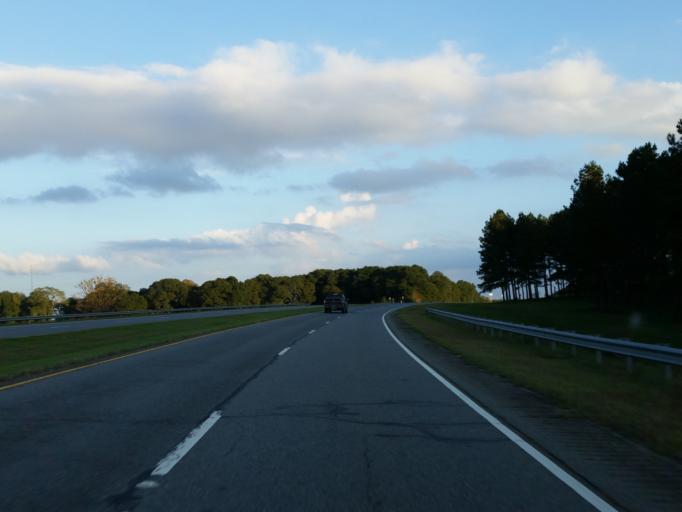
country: US
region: Georgia
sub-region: Houston County
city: Perry
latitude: 32.4403
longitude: -83.7303
